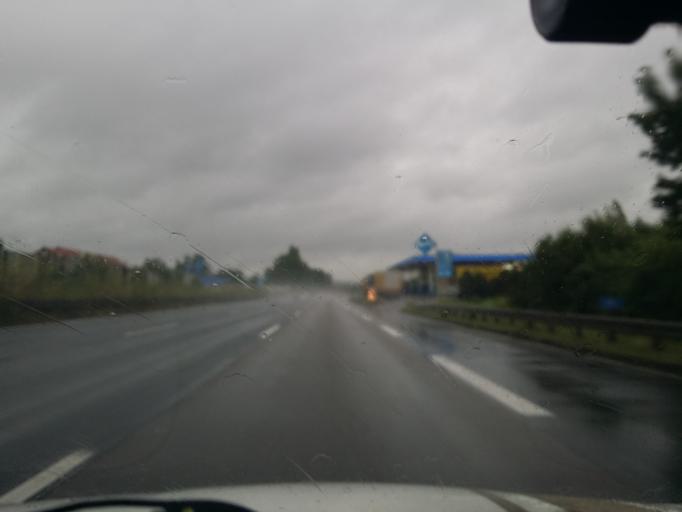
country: DE
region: Hesse
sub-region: Regierungsbezirk Darmstadt
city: Hochheim am Main
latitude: 50.0540
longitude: 8.3098
